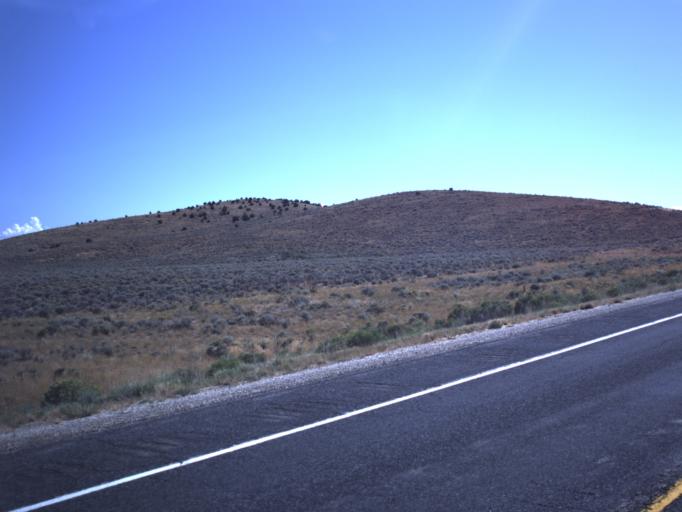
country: US
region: Utah
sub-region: Utah County
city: Eagle Mountain
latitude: 40.0729
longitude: -112.3765
